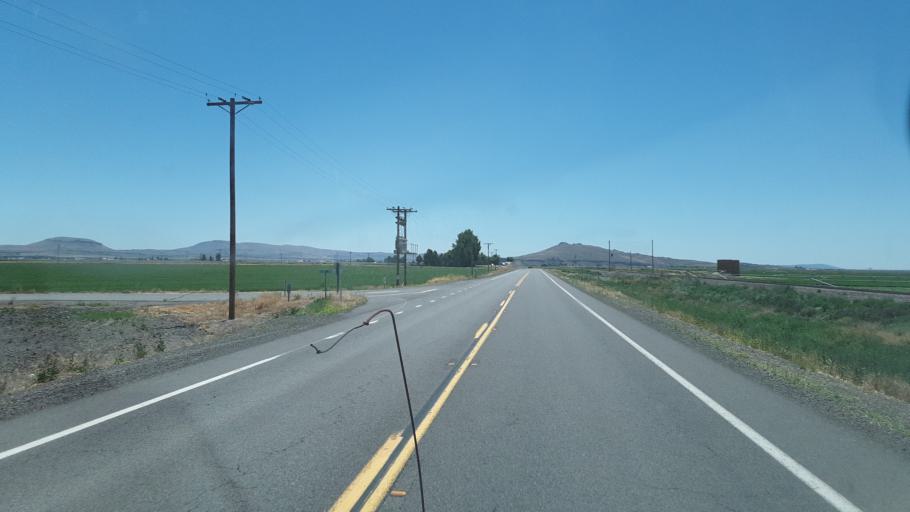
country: US
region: California
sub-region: Siskiyou County
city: Tulelake
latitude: 41.9250
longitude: -121.4383
